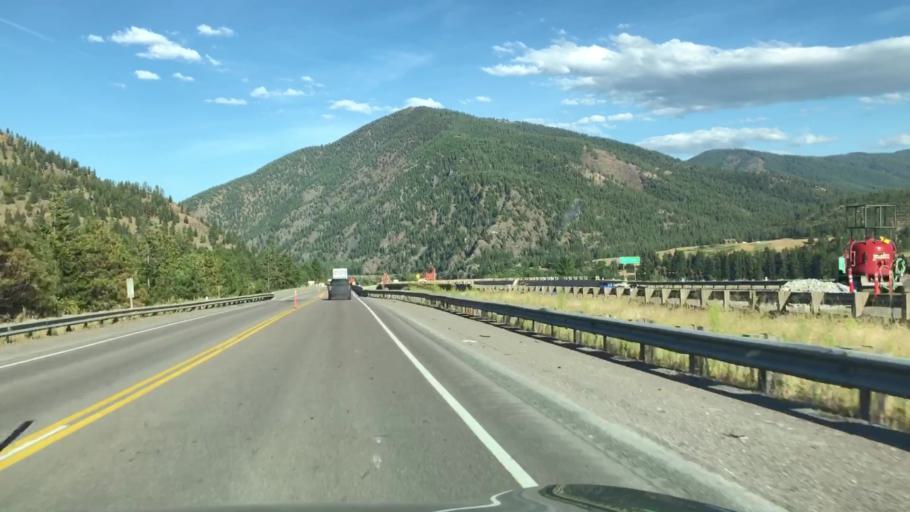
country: US
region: Montana
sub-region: Missoula County
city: Frenchtown
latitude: 47.0043
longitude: -114.5811
